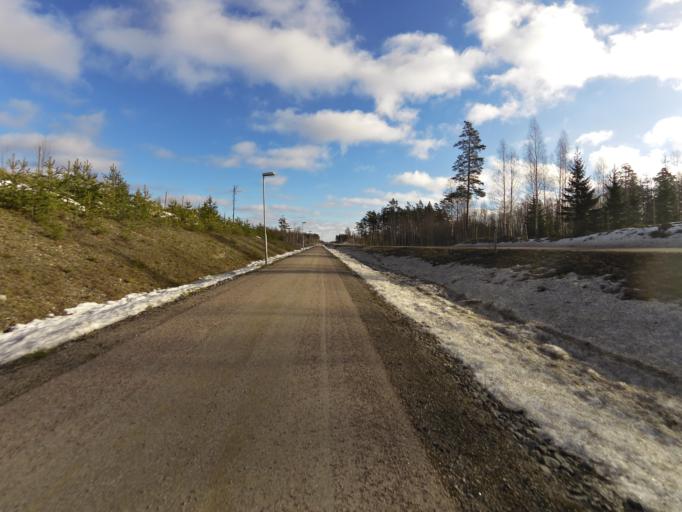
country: SE
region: Uppsala
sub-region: Alvkarleby Kommun
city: Skutskaer
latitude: 60.6481
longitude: 17.2950
